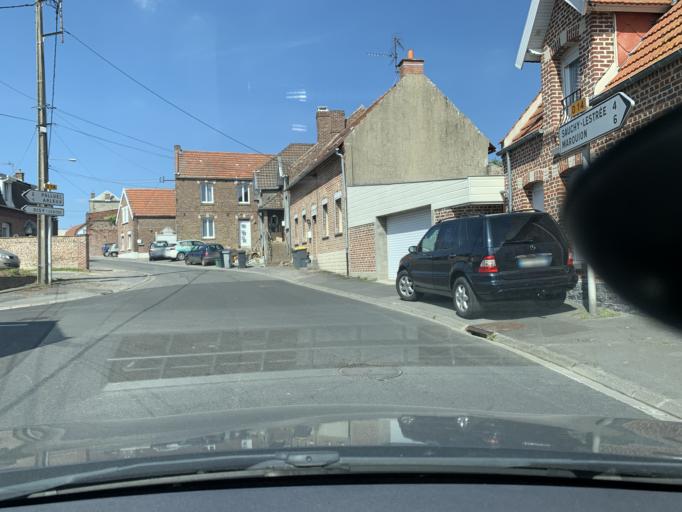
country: FR
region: Nord-Pas-de-Calais
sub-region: Departement du Pas-de-Calais
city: Oisy-le-Verger
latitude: 50.2507
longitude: 3.1189
